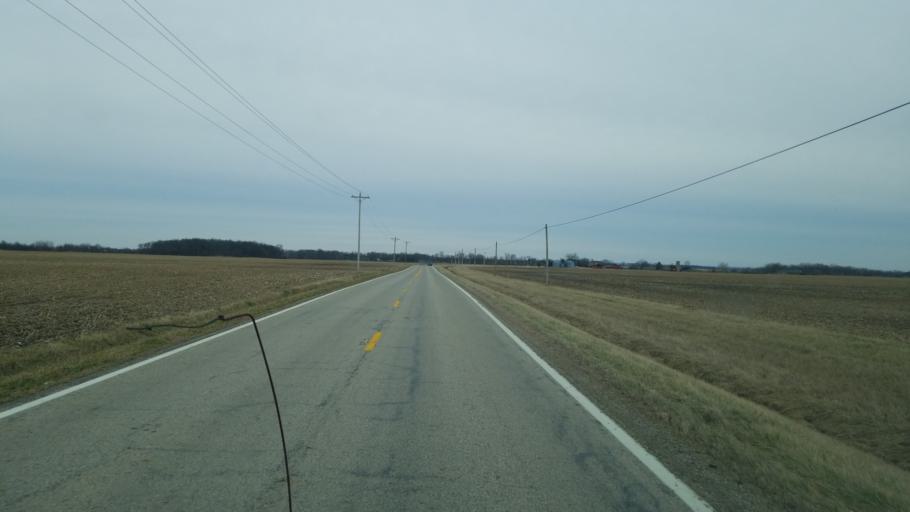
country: US
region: Ohio
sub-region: Pickaway County
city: Williamsport
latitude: 39.5626
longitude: -83.0831
